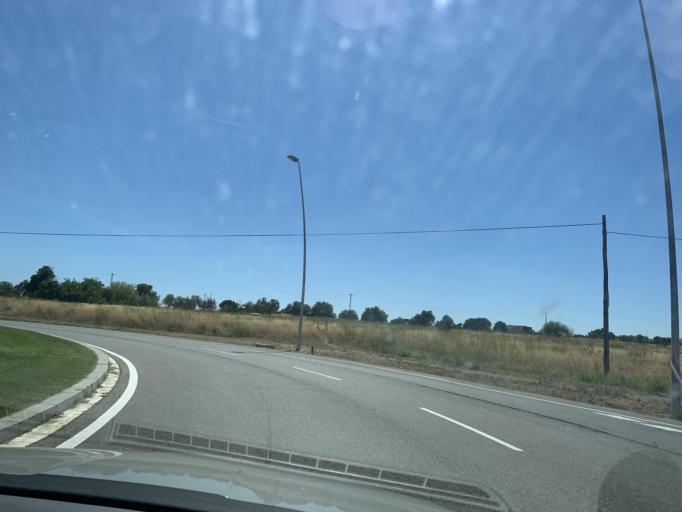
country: ES
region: Catalonia
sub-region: Provincia de Tarragona
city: Reus
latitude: 41.1432
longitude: 1.1275
